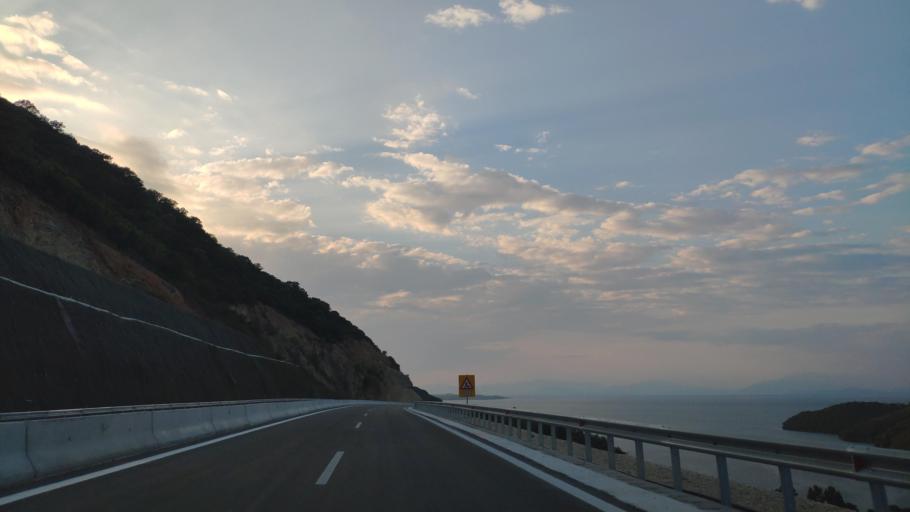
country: GR
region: West Greece
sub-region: Nomos Aitolias kai Akarnanias
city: Katouna
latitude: 38.8581
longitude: 21.0841
